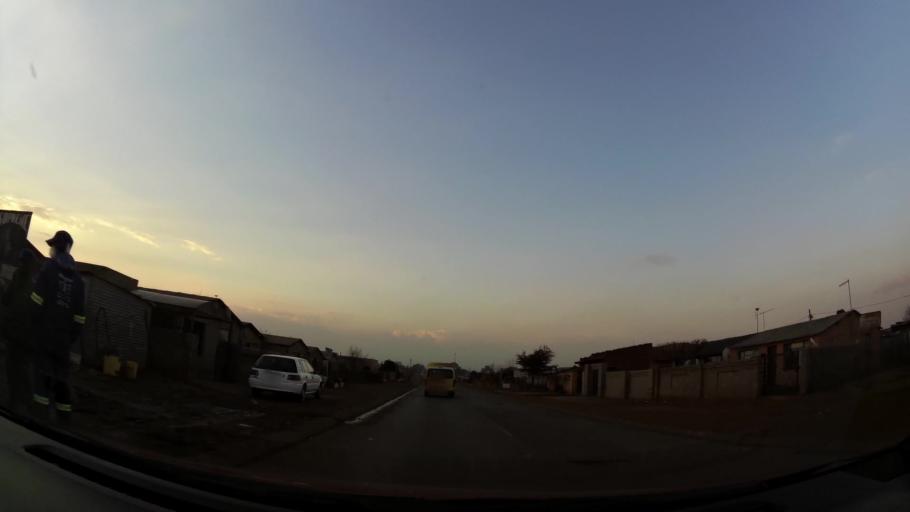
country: ZA
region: Gauteng
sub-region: City of Johannesburg Metropolitan Municipality
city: Orange Farm
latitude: -26.5534
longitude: 27.8633
